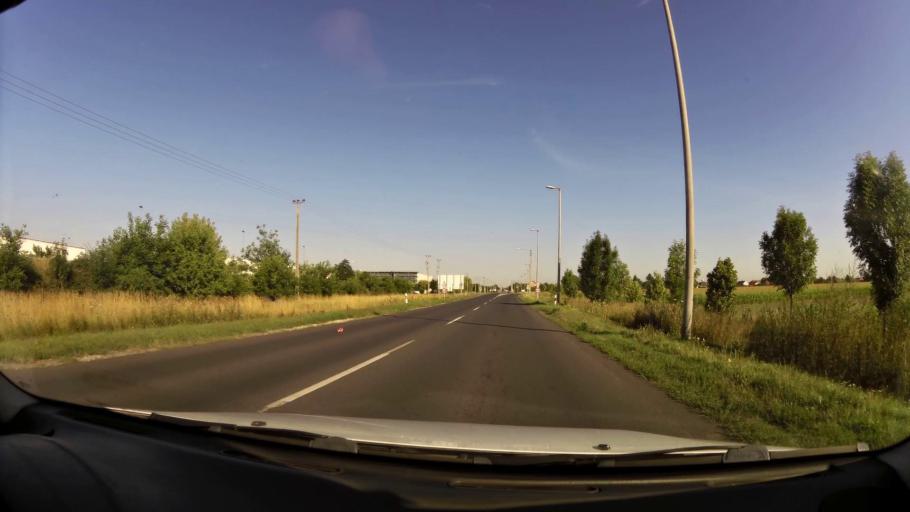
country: HU
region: Pest
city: Ullo
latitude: 47.3765
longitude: 19.3621
